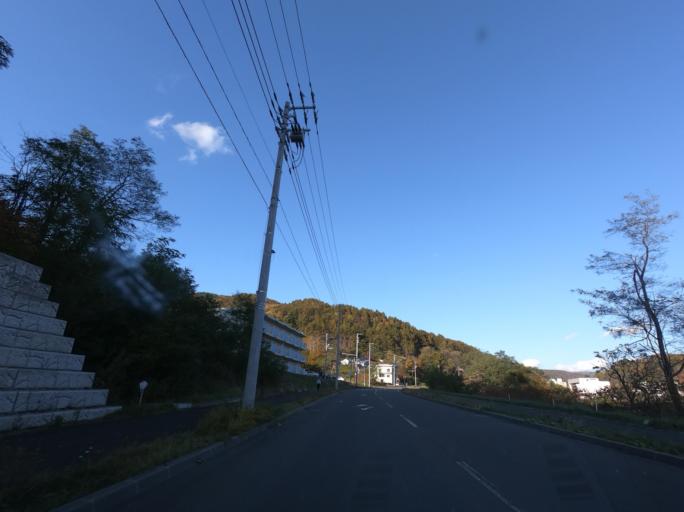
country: JP
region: Hokkaido
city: Iwamizawa
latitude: 43.0531
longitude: 141.9682
